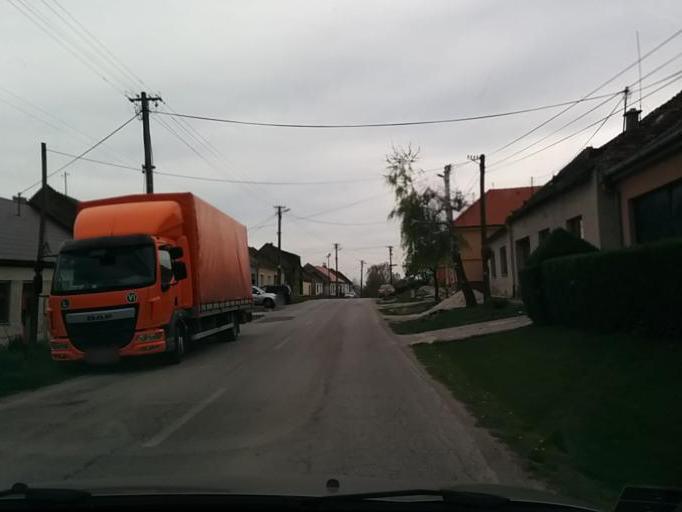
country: SK
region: Bratislavsky
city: Senec
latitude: 48.2531
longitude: 17.4961
